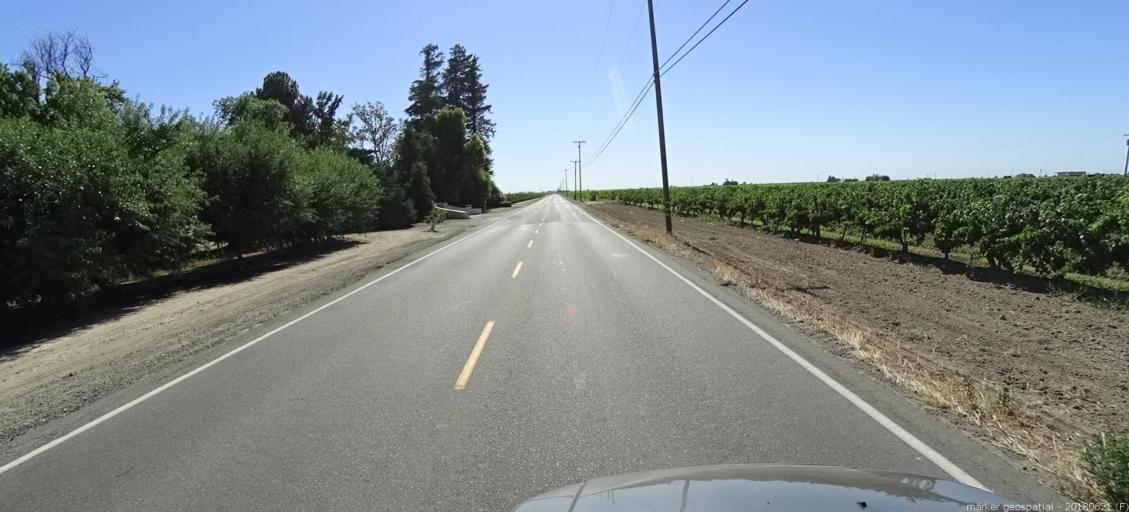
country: US
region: California
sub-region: Fresno County
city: Biola
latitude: 36.8513
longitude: -120.0340
